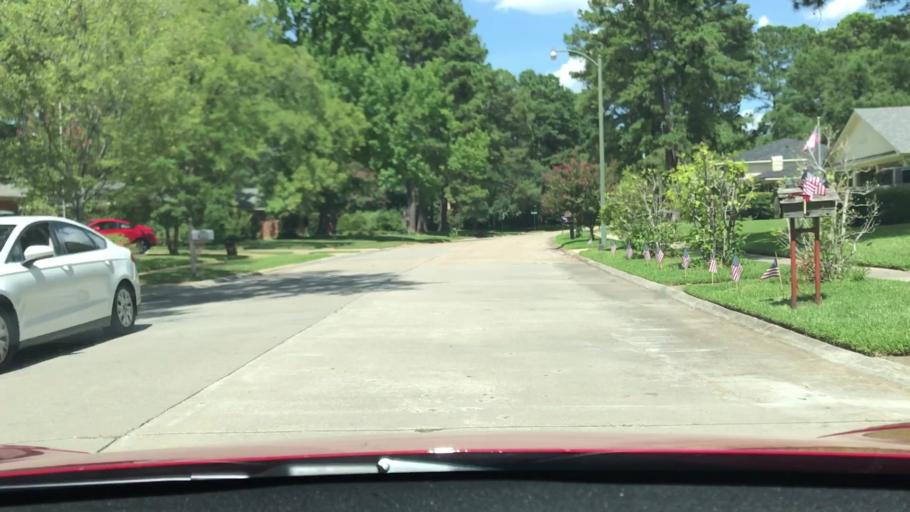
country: US
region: Louisiana
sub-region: Bossier Parish
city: Bossier City
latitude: 32.4226
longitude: -93.7347
